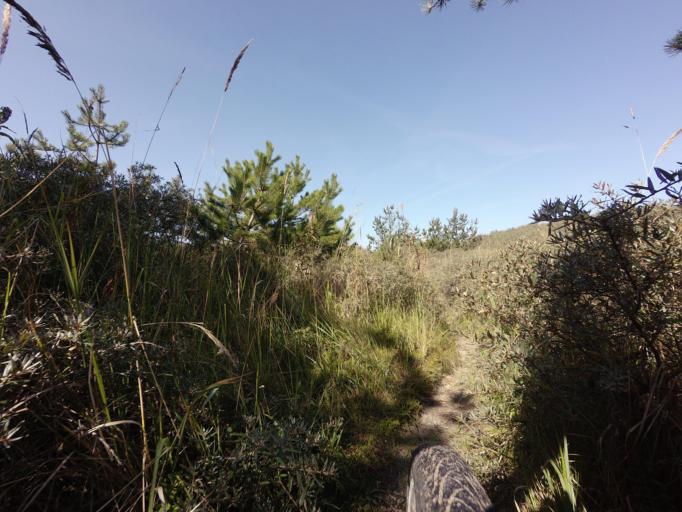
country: DK
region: North Denmark
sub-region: Hjorring Kommune
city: Hirtshals
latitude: 57.5887
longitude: 10.0056
